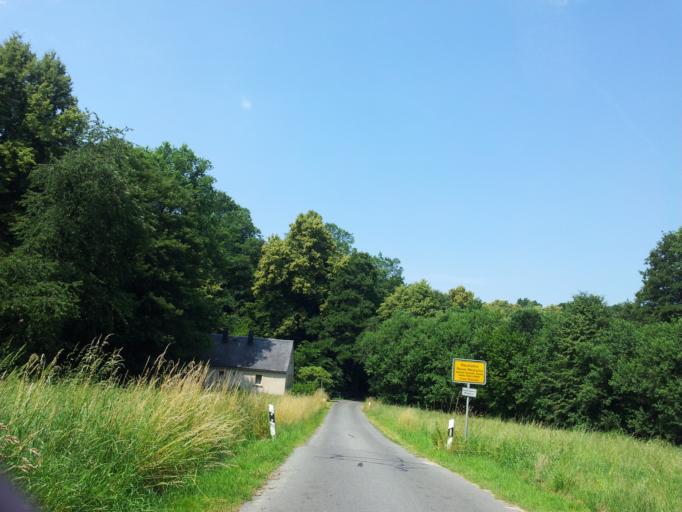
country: DE
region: Saxony
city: Panschwitz-Kuckau
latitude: 51.2134
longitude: 14.2027
